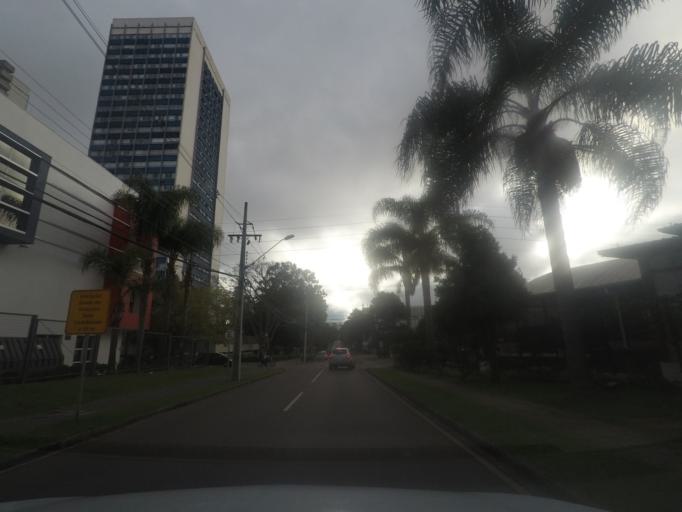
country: BR
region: Parana
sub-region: Curitiba
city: Curitiba
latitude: -25.4300
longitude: -49.2501
